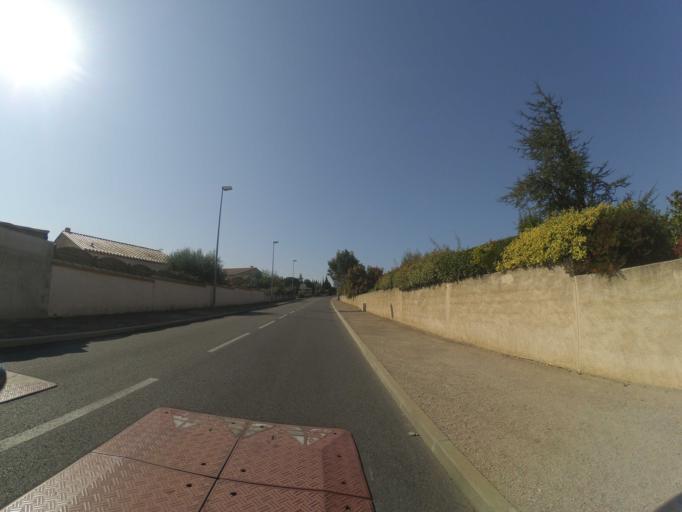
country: FR
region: Languedoc-Roussillon
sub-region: Departement des Pyrenees-Orientales
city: Thuir
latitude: 42.6214
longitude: 2.7511
